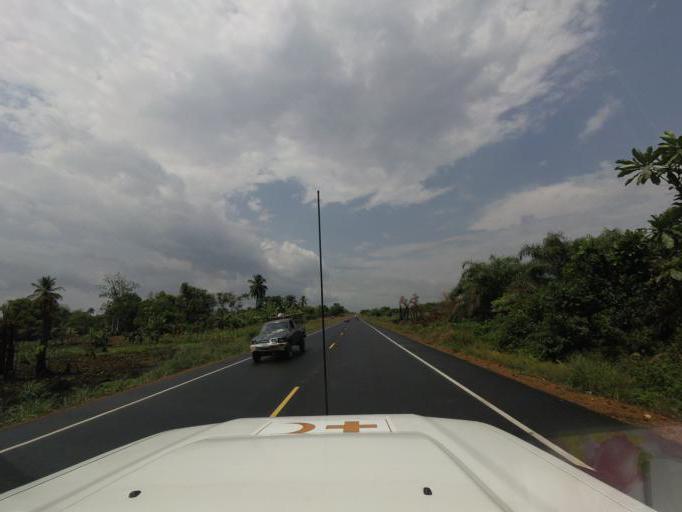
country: LR
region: Montserrado
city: Bensonville City
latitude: 6.4137
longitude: -10.4759
